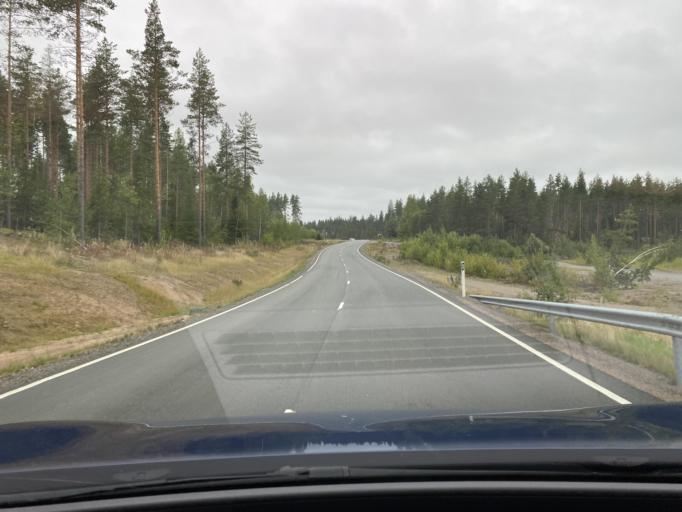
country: FI
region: Kymenlaakso
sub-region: Kouvola
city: Elimaeki
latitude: 60.8735
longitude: 26.5115
